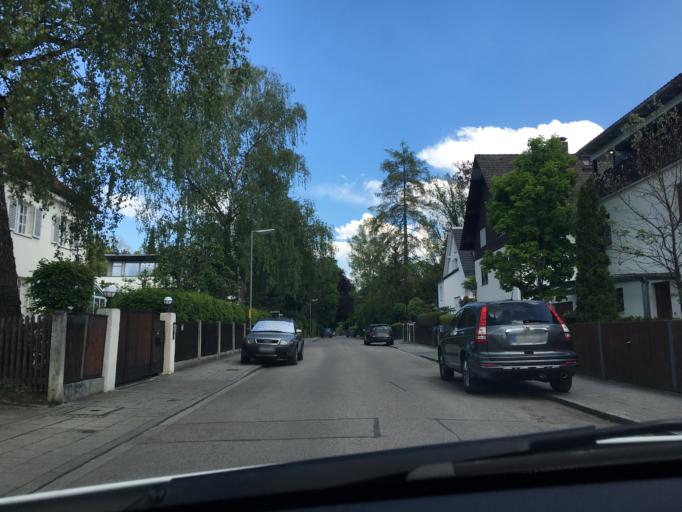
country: DE
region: Bavaria
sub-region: Upper Bavaria
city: Pullach im Isartal
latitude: 48.0784
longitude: 11.5189
